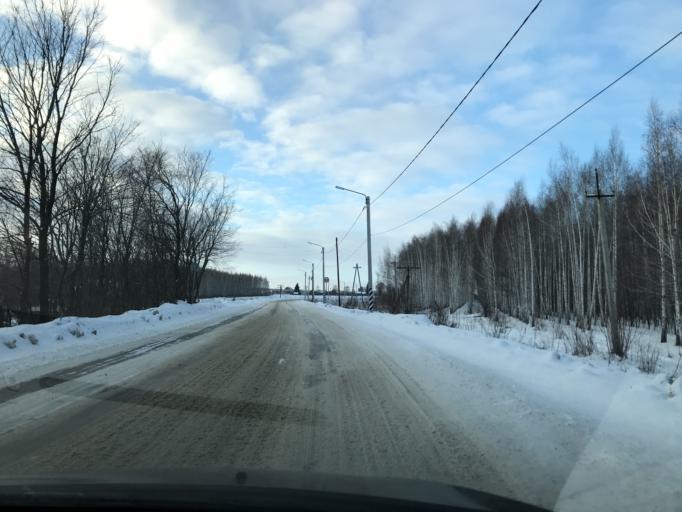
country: RU
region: Ulyanovsk
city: Undory
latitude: 54.6020
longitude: 48.4211
